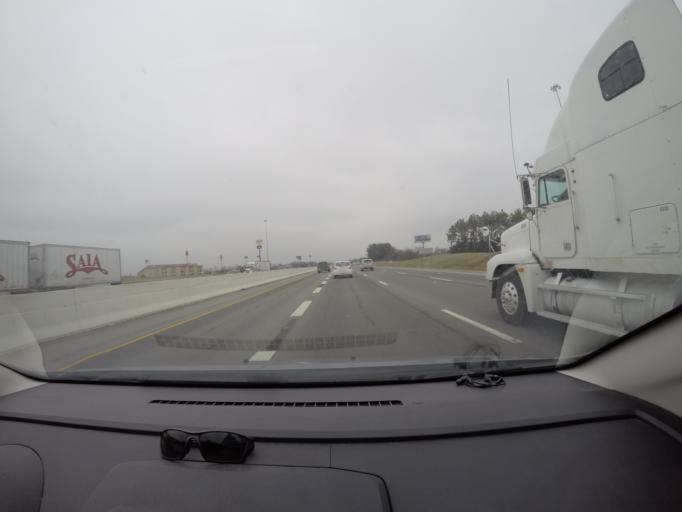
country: US
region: Tennessee
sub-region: Rutherford County
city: Murfreesboro
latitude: 35.8470
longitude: -86.4352
